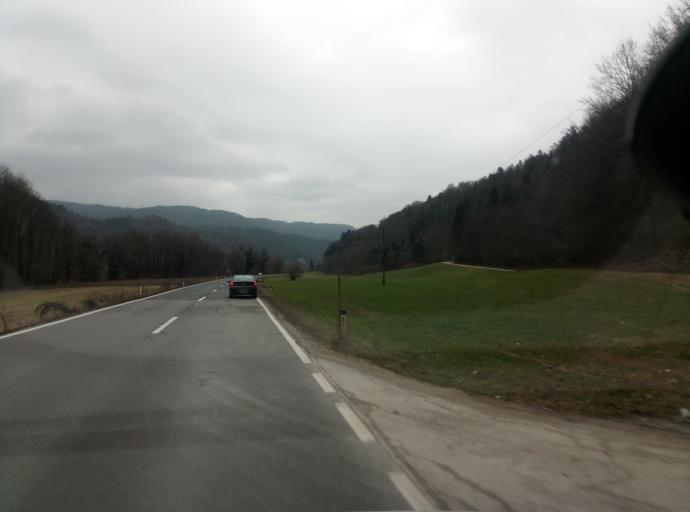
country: SI
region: Smartno pri Litiji
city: Smartno pri Litiji
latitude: 46.0763
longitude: 14.8704
